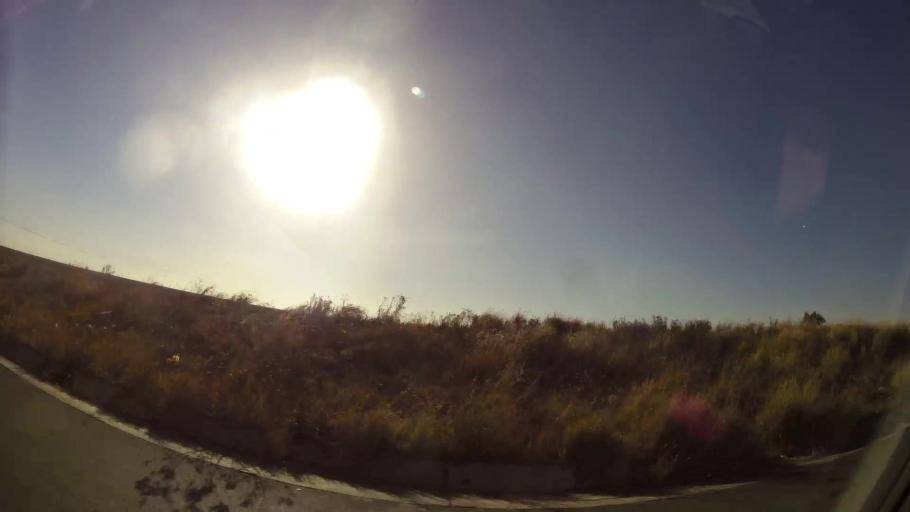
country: ZA
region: Gauteng
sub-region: City of Johannesburg Metropolitan Municipality
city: Diepsloot
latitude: -25.9448
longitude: 27.9737
